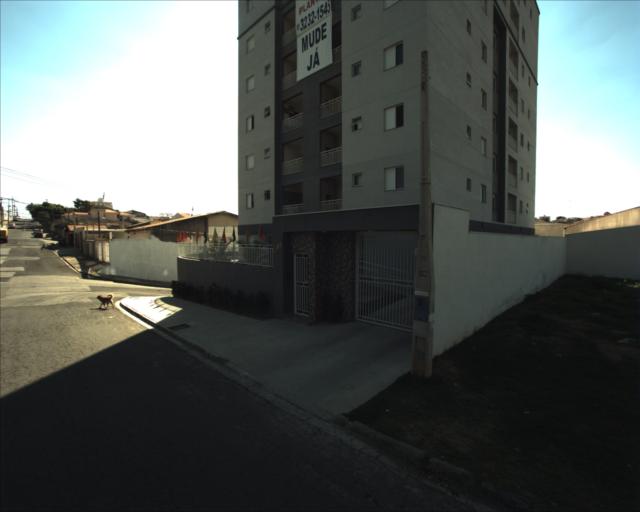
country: BR
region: Sao Paulo
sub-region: Sorocaba
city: Sorocaba
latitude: -23.5118
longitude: -47.4321
